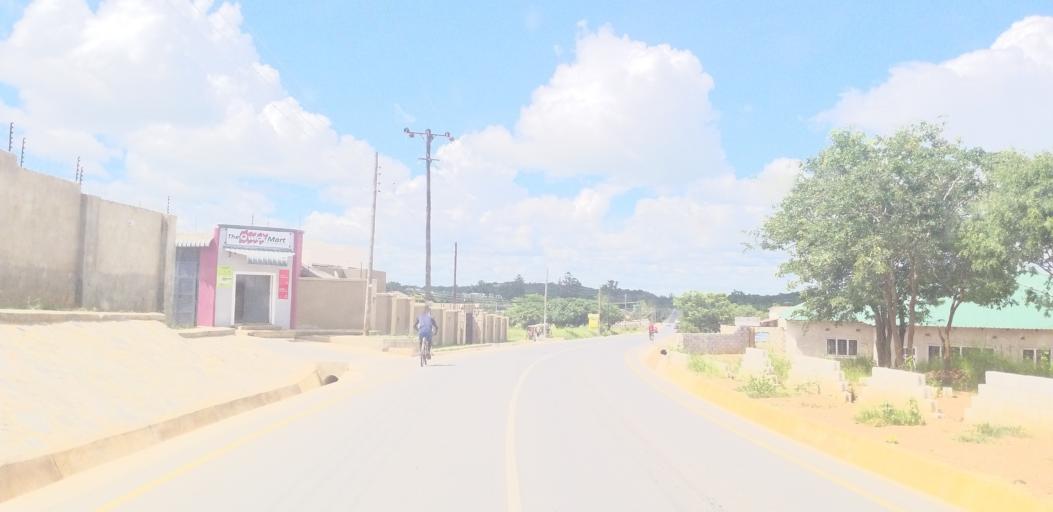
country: ZM
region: Lusaka
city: Lusaka
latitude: -15.3410
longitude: 28.3283
